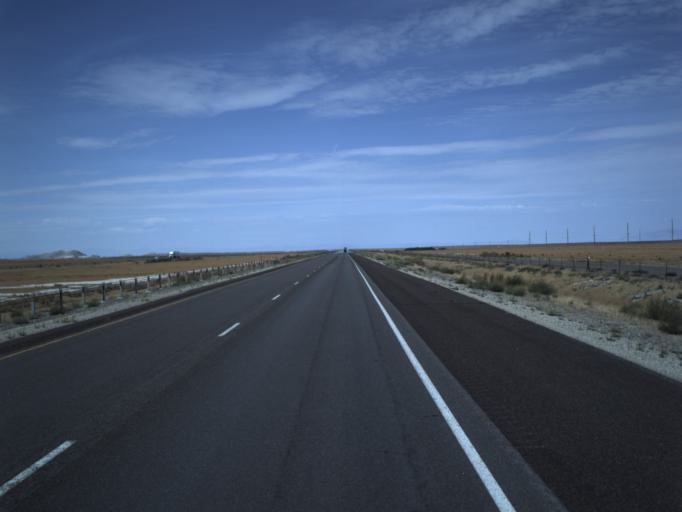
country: US
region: Utah
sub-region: Tooele County
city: Grantsville
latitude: 40.7266
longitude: -113.1900
